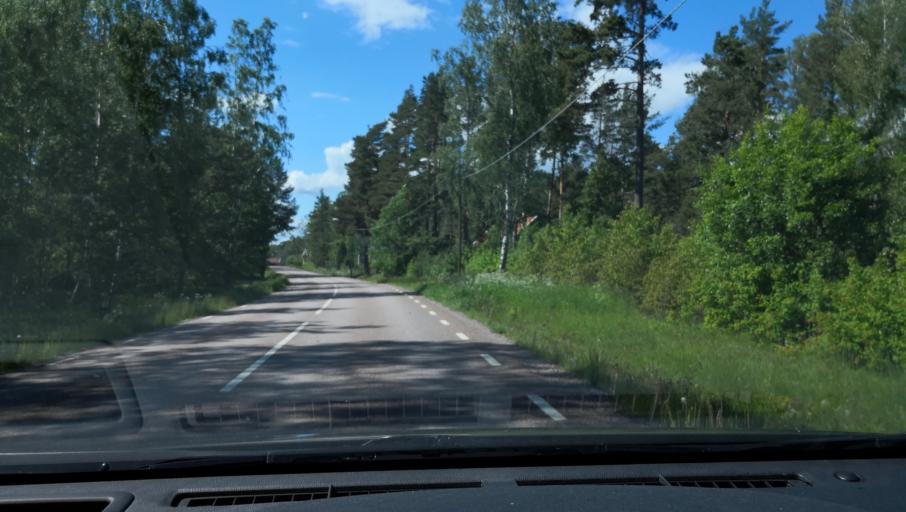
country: SE
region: Vaestmanland
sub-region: Kungsors Kommun
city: Kungsoer
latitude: 59.2910
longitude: 16.0550
